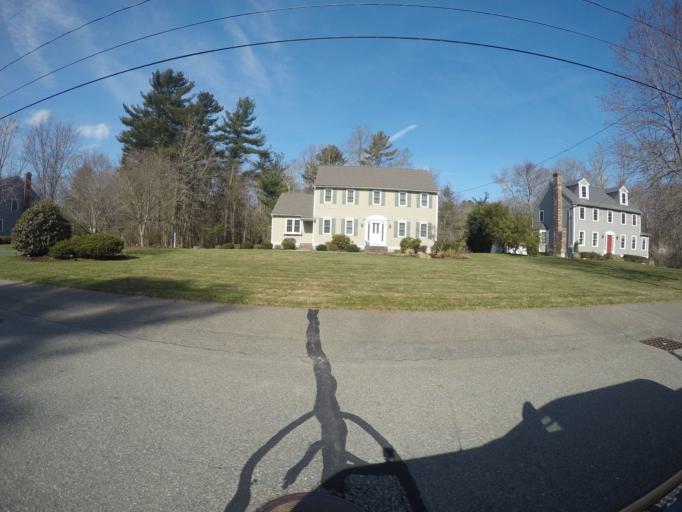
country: US
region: Massachusetts
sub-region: Bristol County
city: Easton
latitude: 42.0190
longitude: -71.1487
